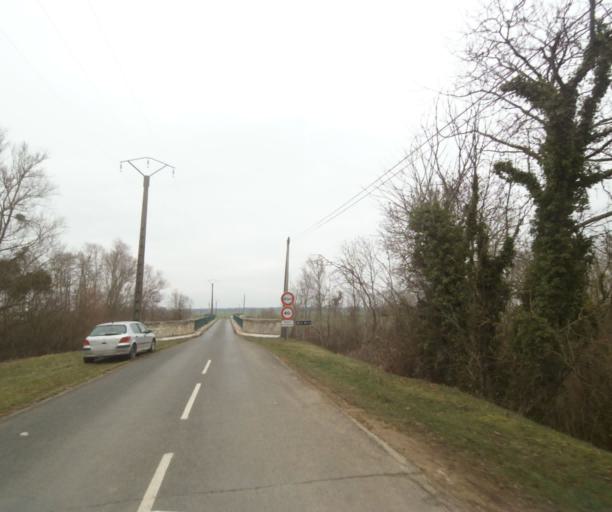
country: FR
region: Champagne-Ardenne
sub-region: Departement de la Haute-Marne
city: Villiers-en-Lieu
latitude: 48.6423
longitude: 4.7677
